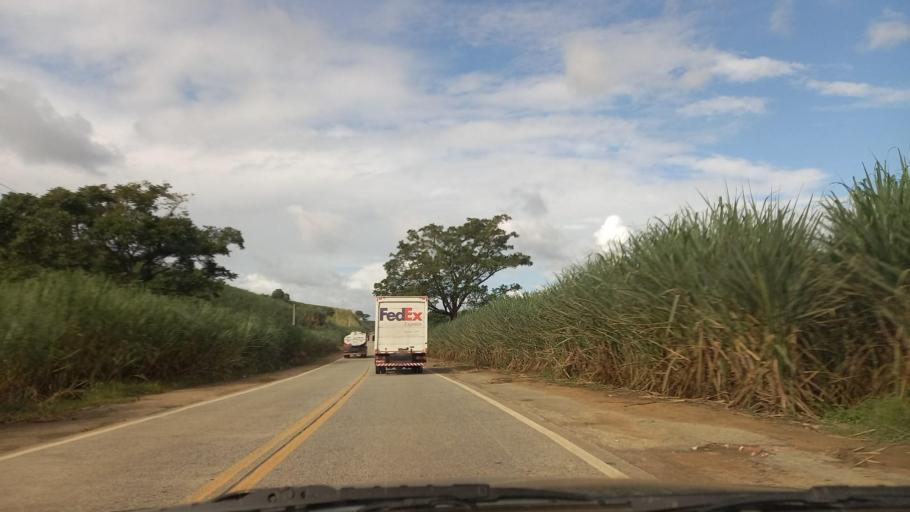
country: BR
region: Pernambuco
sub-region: Palmares
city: Palmares
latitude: -8.6947
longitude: -35.6477
